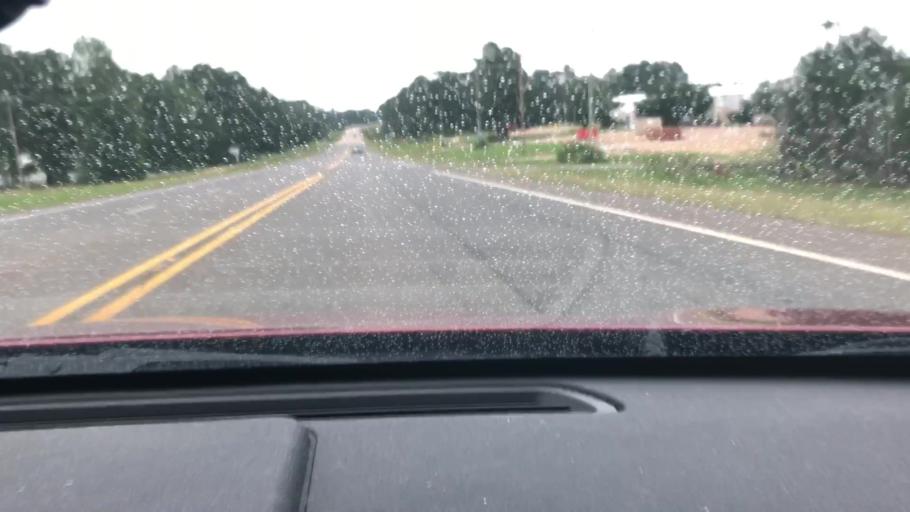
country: US
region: Arkansas
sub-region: Lafayette County
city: Lewisville
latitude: 33.3597
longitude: -93.5559
